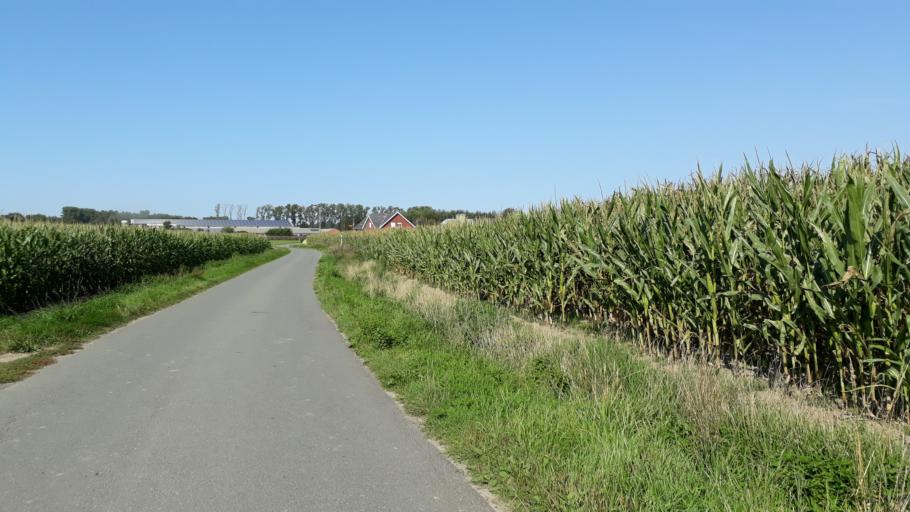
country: BE
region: Flanders
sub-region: Provincie West-Vlaanderen
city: Kortemark
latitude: 51.0566
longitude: 3.0562
